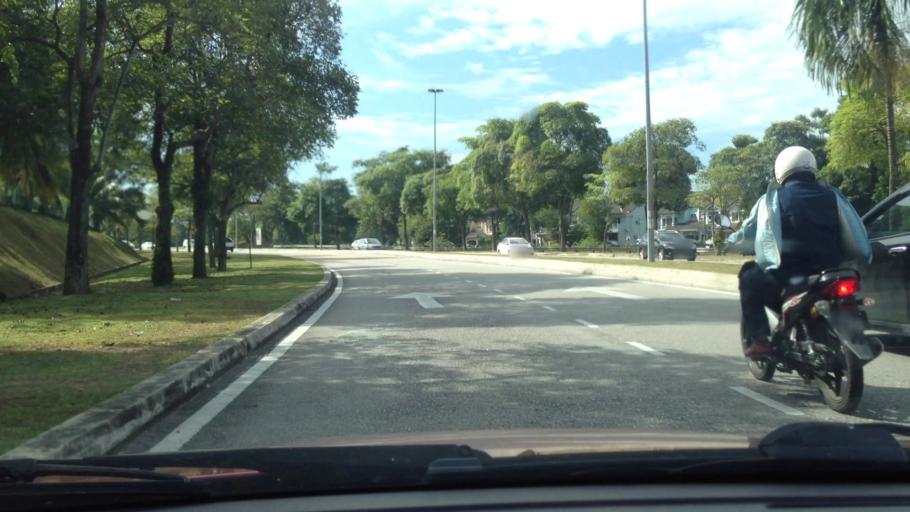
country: MY
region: Selangor
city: Subang Jaya
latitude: 3.0456
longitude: 101.5704
